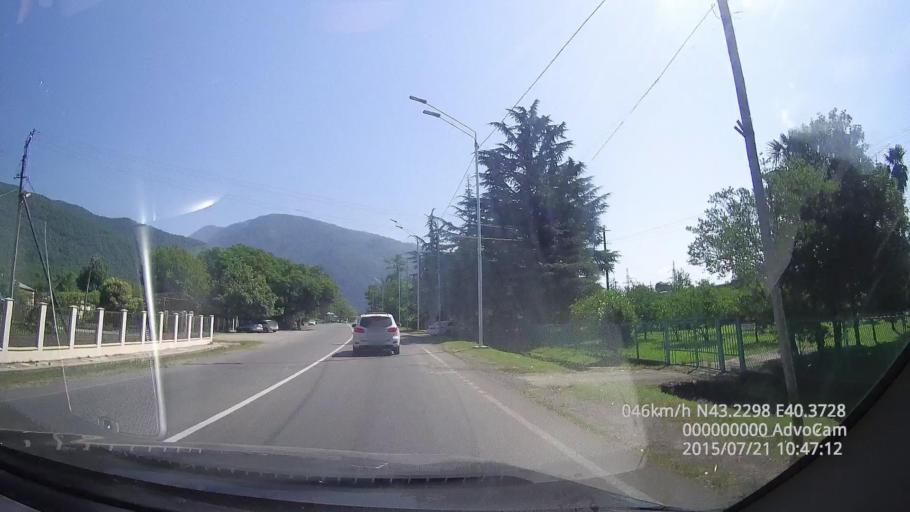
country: GE
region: Abkhazia
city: Bich'vinta
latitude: 43.2299
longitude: 40.3730
